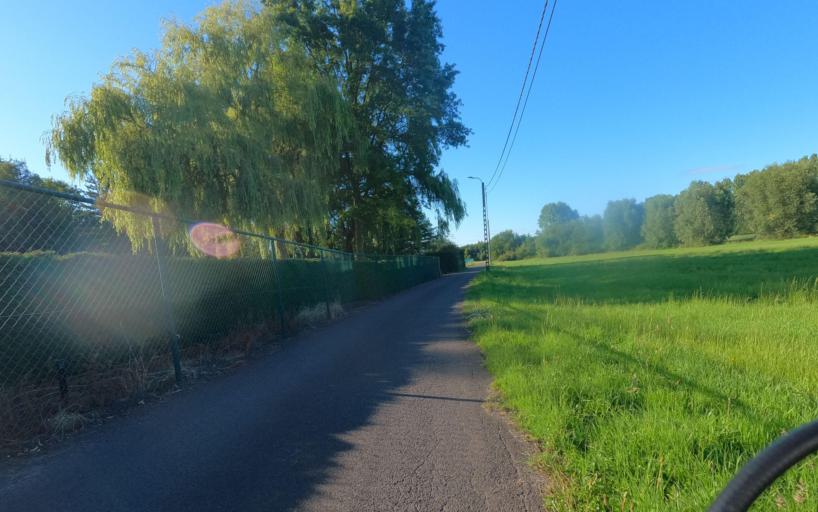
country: BE
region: Flanders
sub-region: Provincie Antwerpen
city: Putte
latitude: 51.0729
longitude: 4.6451
